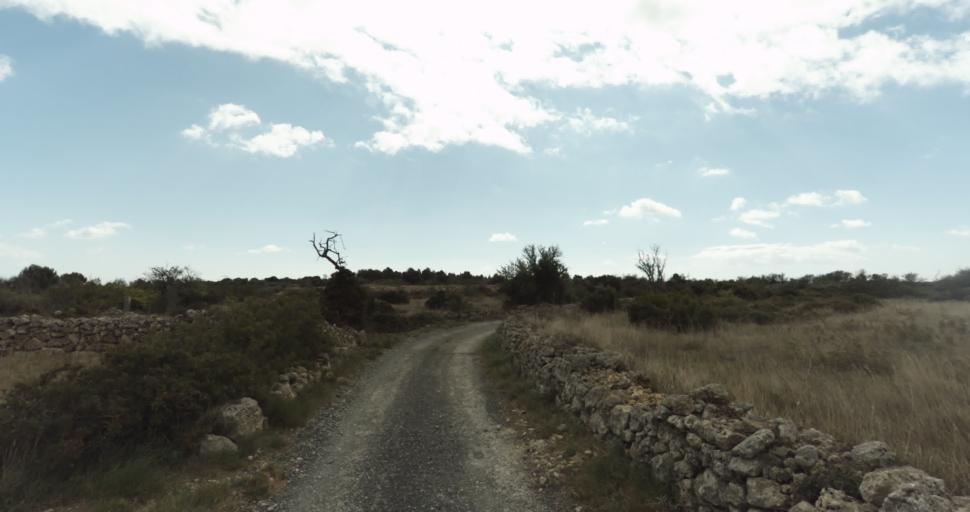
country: FR
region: Languedoc-Roussillon
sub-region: Departement de l'Aude
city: Leucate
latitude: 42.9186
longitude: 3.0390
